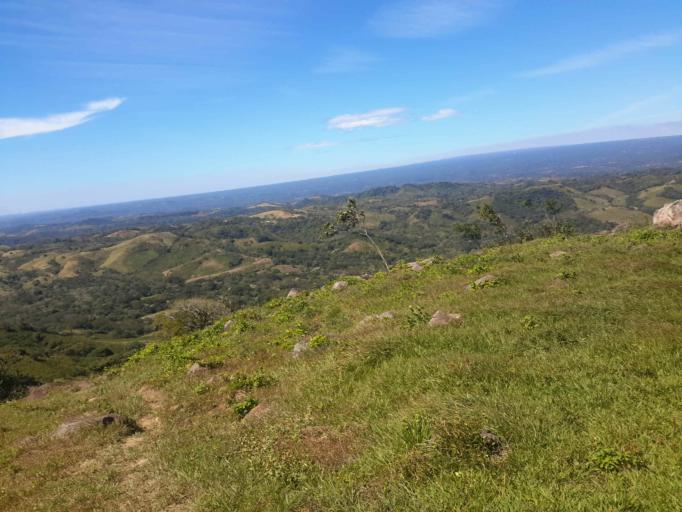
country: NI
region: Carazo
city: Santa Teresa
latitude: 11.6647
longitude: -86.1642
